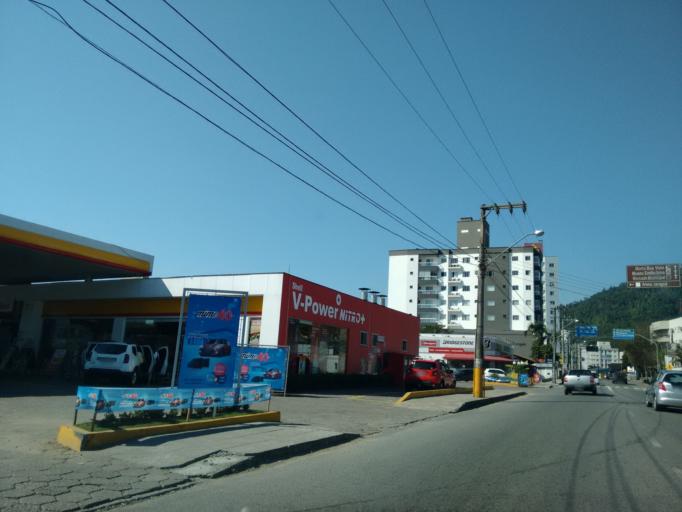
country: BR
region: Santa Catarina
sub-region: Jaragua Do Sul
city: Jaragua do Sul
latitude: -26.5001
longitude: -49.0878
